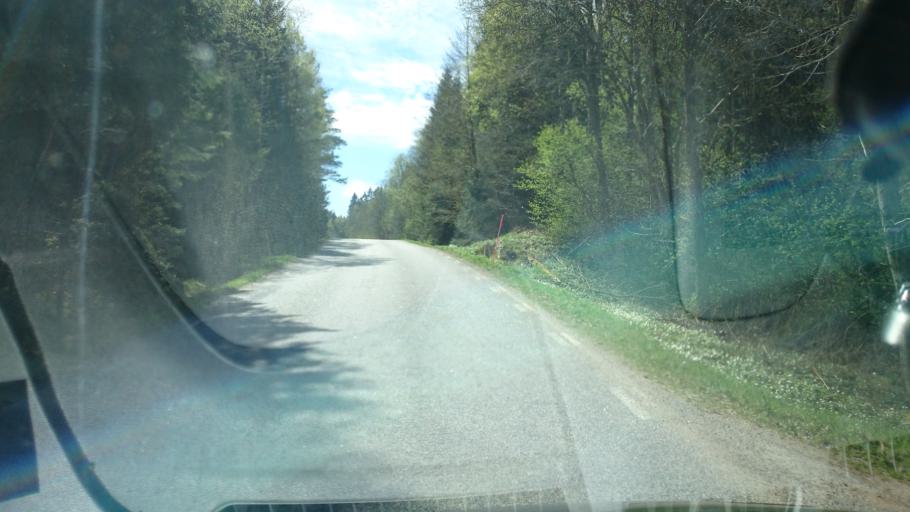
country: SE
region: Vaestra Goetaland
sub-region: Munkedals Kommun
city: Munkedal
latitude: 58.4117
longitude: 11.6737
